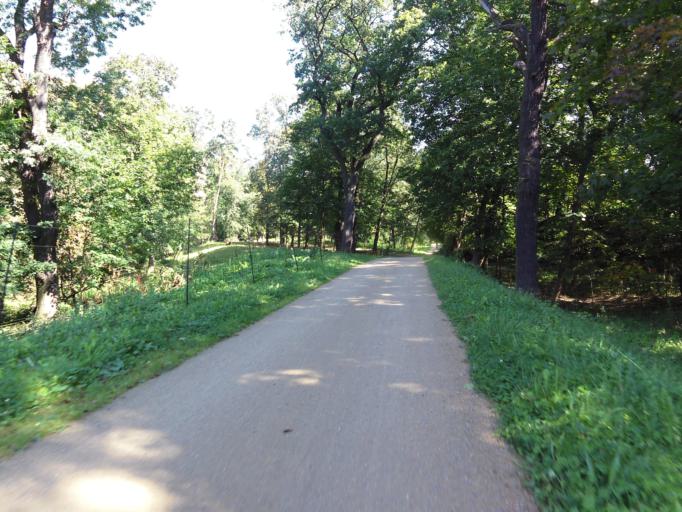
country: DE
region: Saxony-Anhalt
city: Dessau
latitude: 51.8577
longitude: 12.2309
